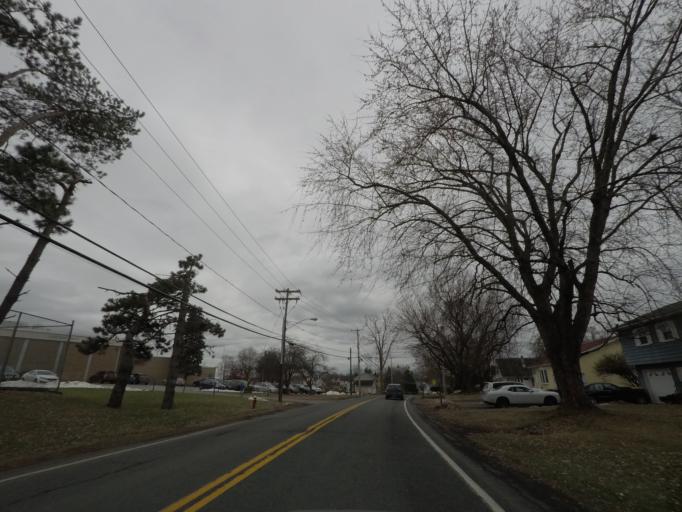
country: US
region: New York
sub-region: Schenectady County
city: Niskayuna
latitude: 42.7645
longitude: -73.7792
